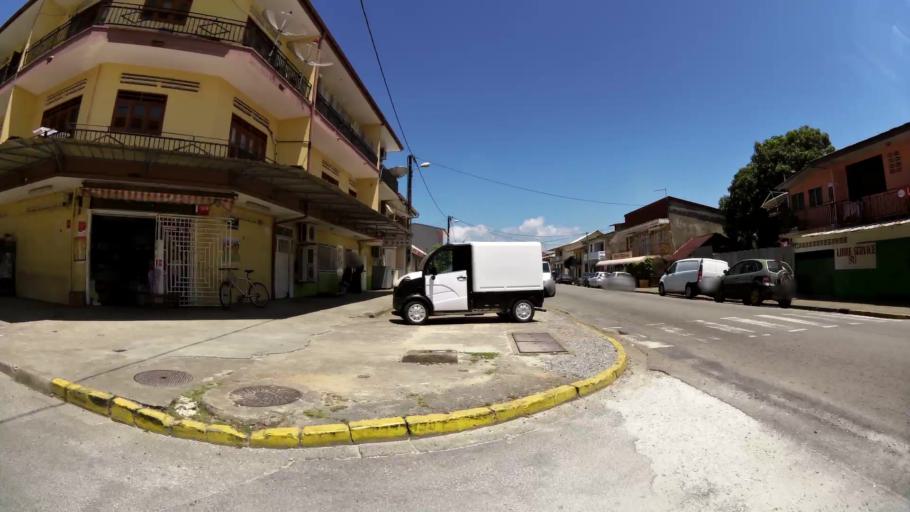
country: GF
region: Guyane
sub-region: Guyane
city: Cayenne
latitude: 4.9346
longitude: -52.3307
